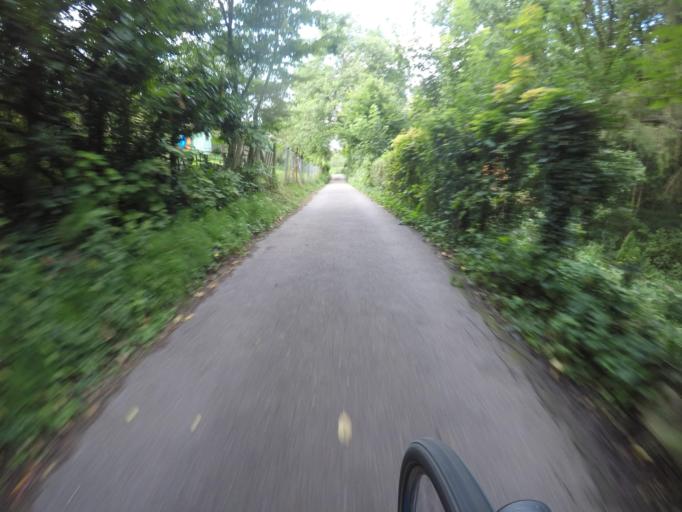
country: DE
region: Baden-Wuerttemberg
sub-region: Regierungsbezirk Stuttgart
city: Ostfildern
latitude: 48.7506
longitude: 9.2470
